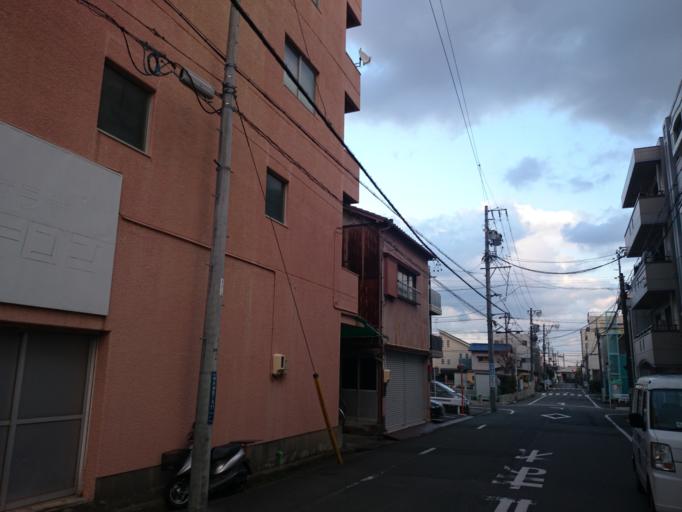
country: JP
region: Shizuoka
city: Shizuoka-shi
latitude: 34.9657
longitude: 138.3757
